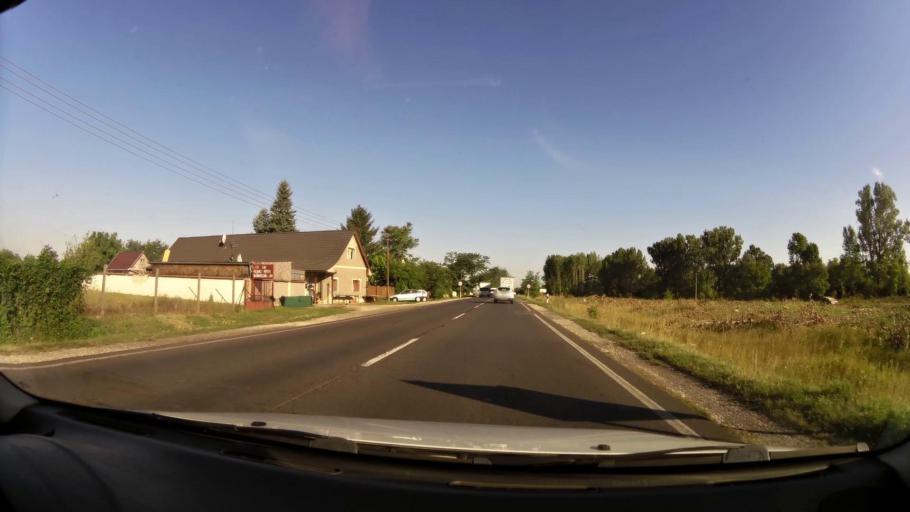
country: HU
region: Pest
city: Pilis
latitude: 47.2754
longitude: 19.5603
